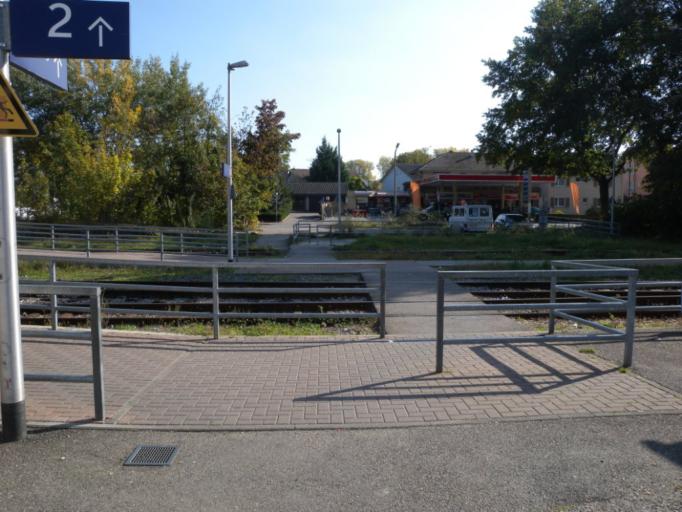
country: DE
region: Baden-Wuerttemberg
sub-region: Freiburg Region
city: Breisach am Rhein
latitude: 48.0267
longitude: 7.5890
